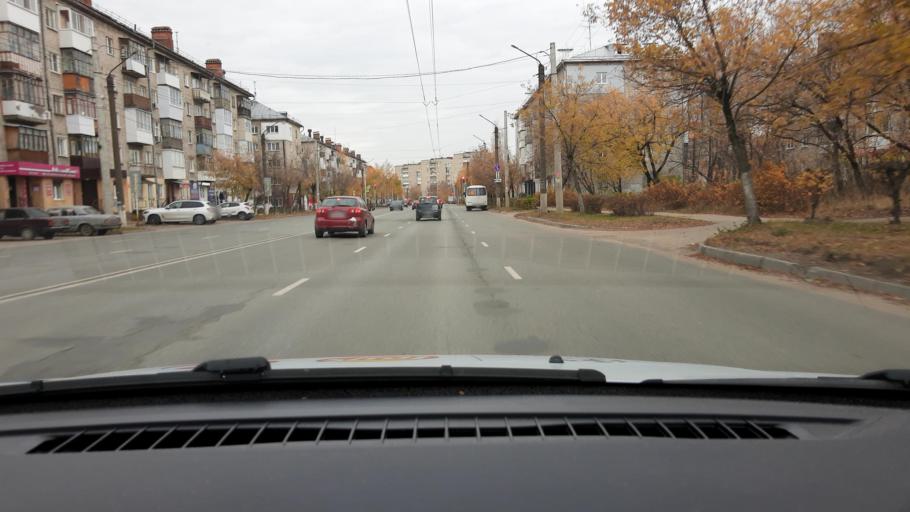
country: RU
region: Nizjnij Novgorod
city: Dzerzhinsk
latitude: 56.2424
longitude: 43.4392
